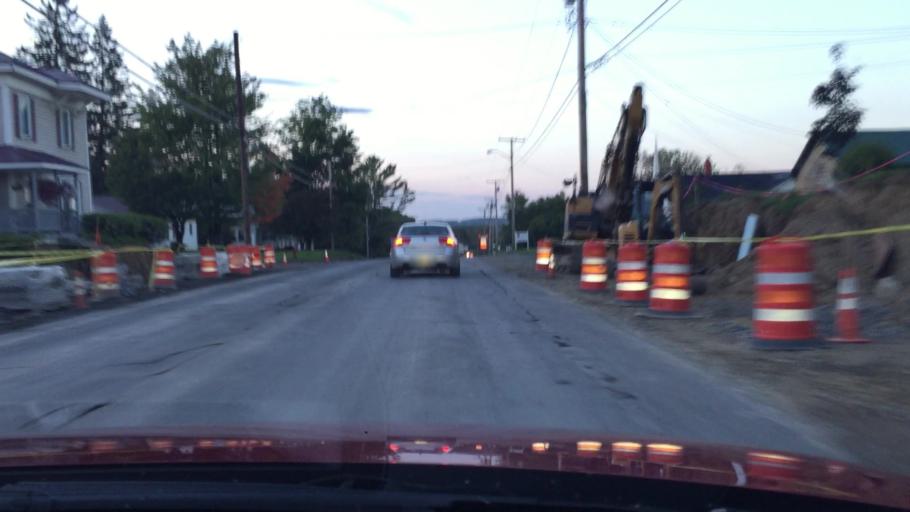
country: US
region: Maine
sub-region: Aroostook County
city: Easton
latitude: 46.5066
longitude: -67.8685
